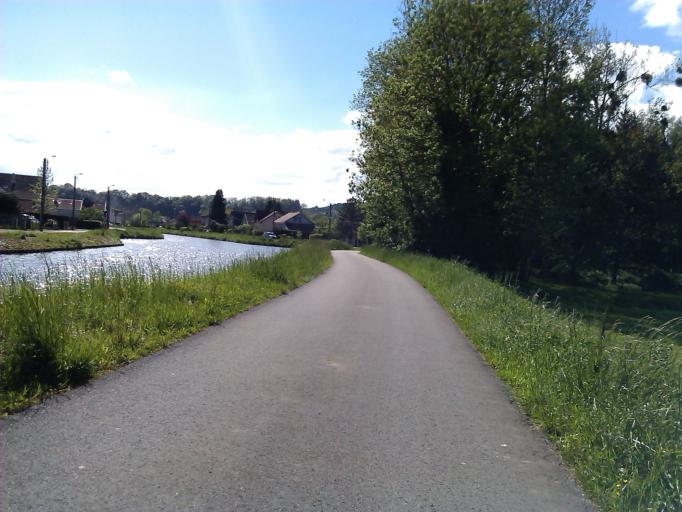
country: FR
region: Franche-Comte
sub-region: Departement du Doubs
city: Montenois
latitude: 47.4522
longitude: 6.5910
